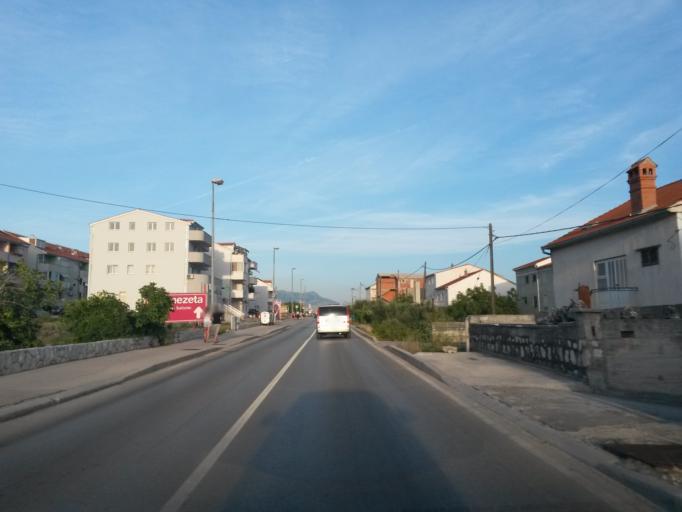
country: HR
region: Splitsko-Dalmatinska
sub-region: Grad Split
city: Split
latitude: 43.5524
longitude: 16.3738
